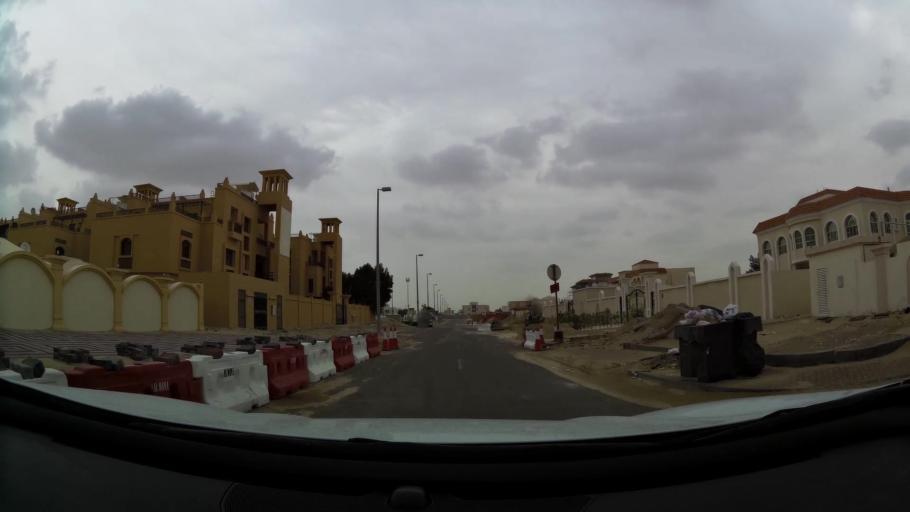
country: AE
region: Abu Dhabi
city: Abu Dhabi
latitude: 24.3724
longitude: 54.6272
